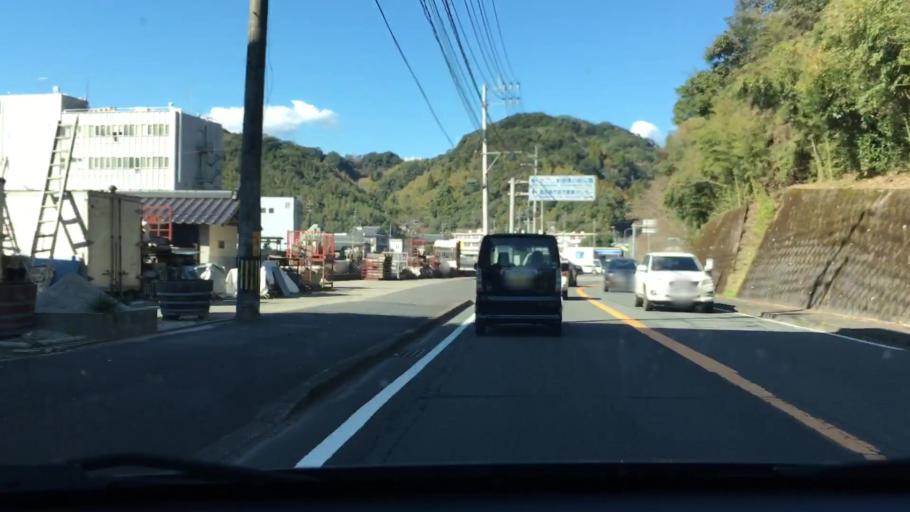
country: JP
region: Kagoshima
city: Kagoshima-shi
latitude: 31.6404
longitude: 130.5162
